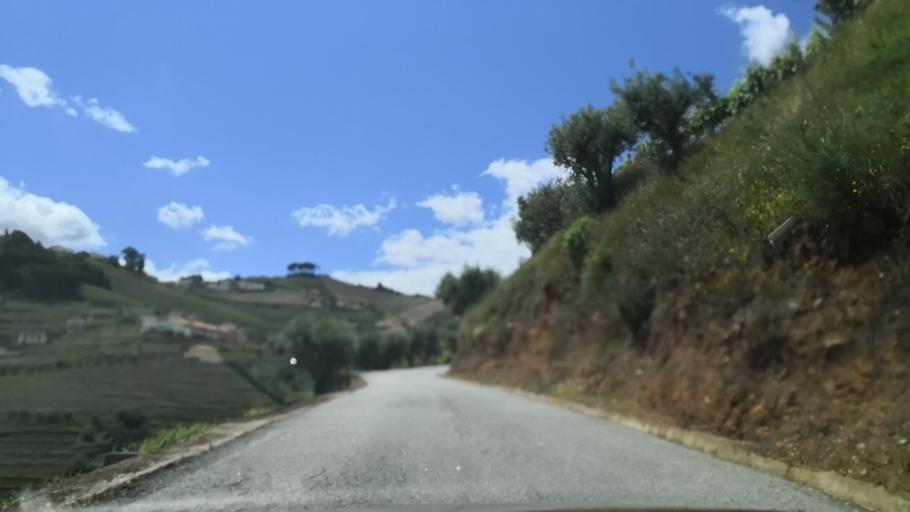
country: PT
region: Vila Real
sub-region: Santa Marta de Penaguiao
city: Santa Marta de Penaguiao
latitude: 41.2282
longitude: -7.7832
